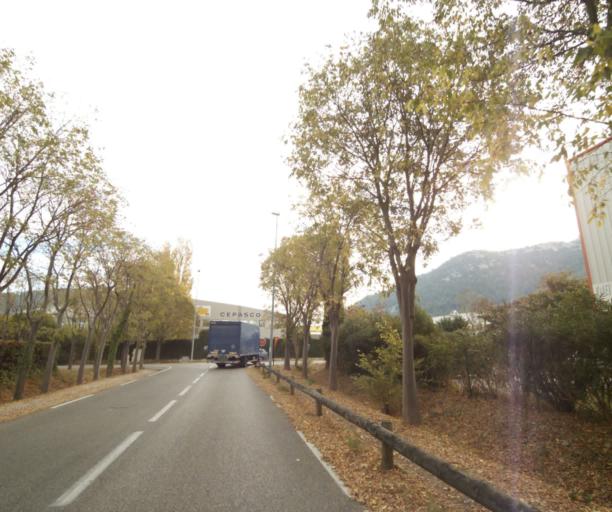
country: FR
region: Provence-Alpes-Cote d'Azur
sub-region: Departement des Bouches-du-Rhone
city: Gemenos
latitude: 43.2798
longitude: 5.6173
